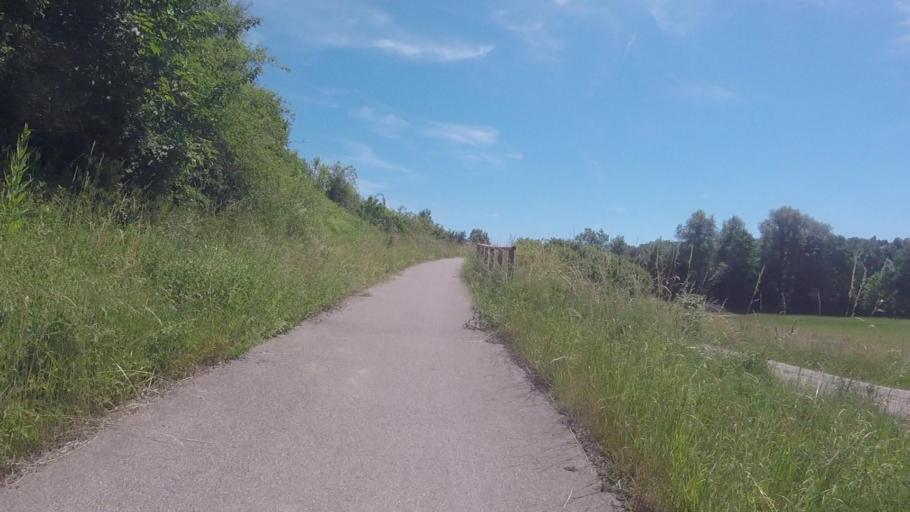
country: DE
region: Baden-Wuerttemberg
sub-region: Regierungsbezirk Stuttgart
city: Erdmannhausen
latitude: 48.9518
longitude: 9.3001
